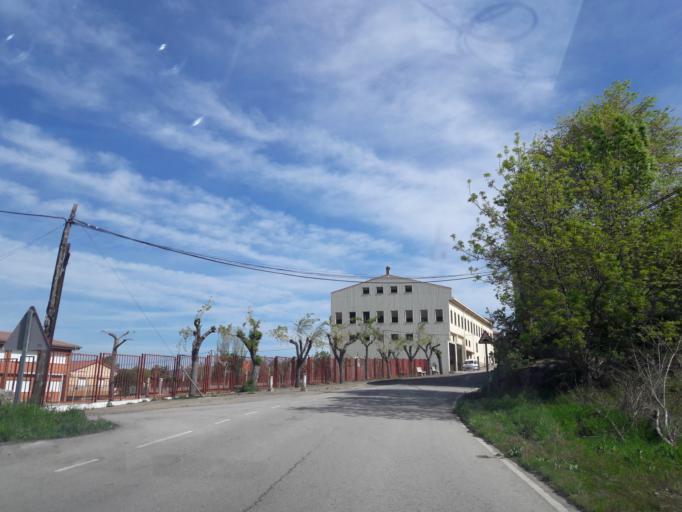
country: ES
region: Castille and Leon
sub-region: Provincia de Salamanca
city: Ledrada
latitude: 40.4639
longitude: -5.7230
